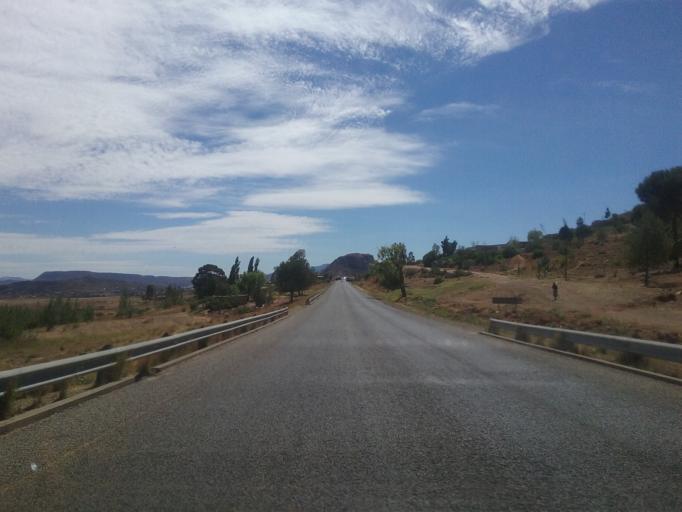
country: LS
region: Mohale's Hoek District
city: Mohale's Hoek
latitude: -30.1849
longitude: 27.4231
